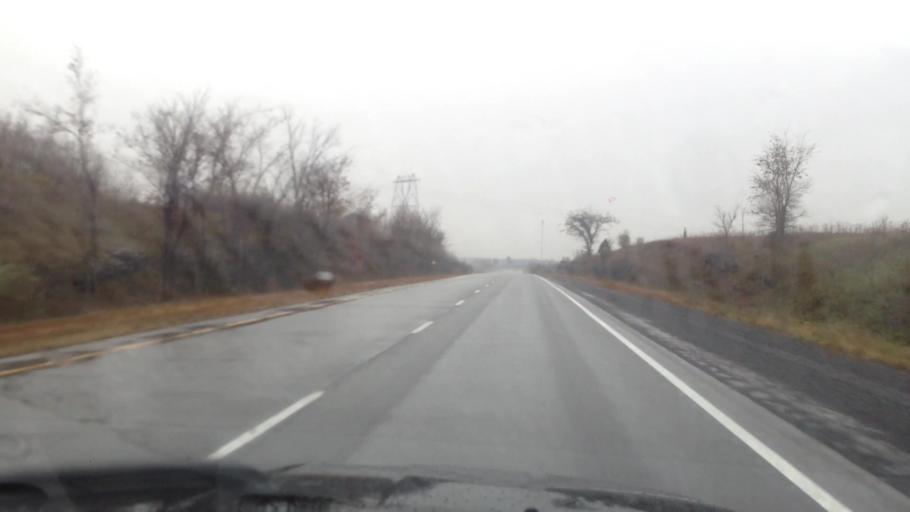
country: CA
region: Ontario
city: Casselman
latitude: 45.3727
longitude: -74.8478
